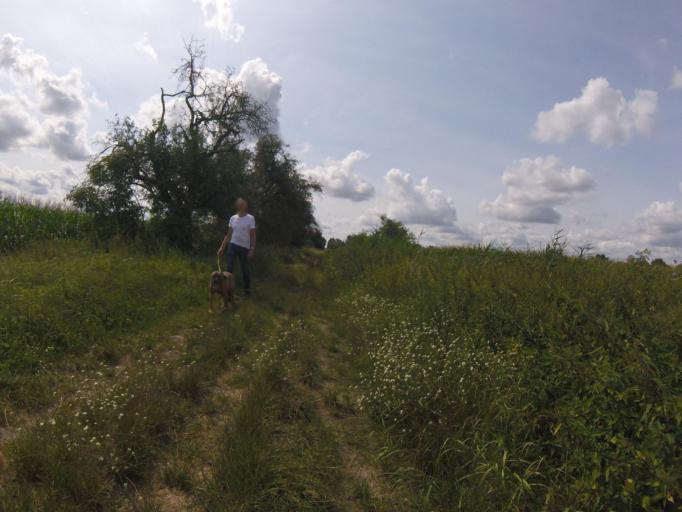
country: DE
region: Brandenburg
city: Mittenwalde
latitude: 52.2890
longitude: 13.5066
